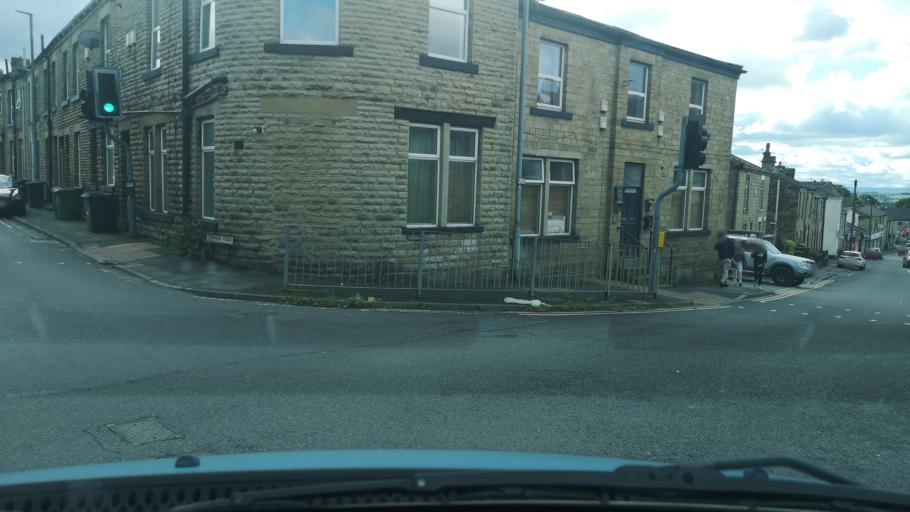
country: GB
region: England
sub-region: Kirklees
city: Heckmondwike
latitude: 53.7107
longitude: -1.6597
